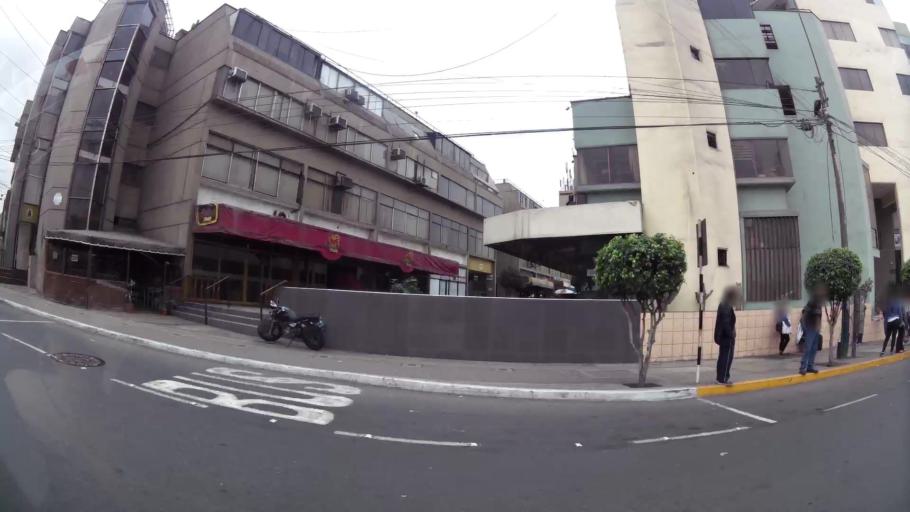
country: PE
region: Lima
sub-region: Lima
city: Surco
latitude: -12.1117
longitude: -76.9932
